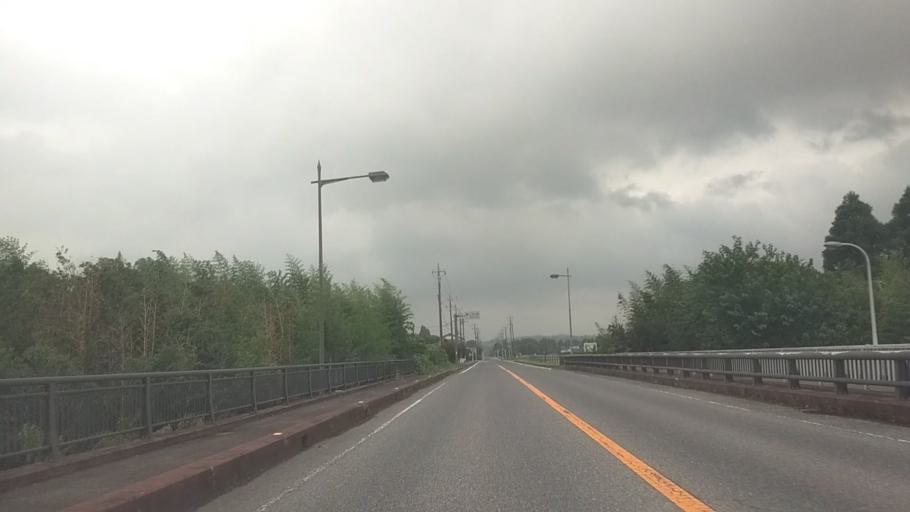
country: JP
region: Chiba
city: Ohara
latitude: 35.2858
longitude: 140.2657
